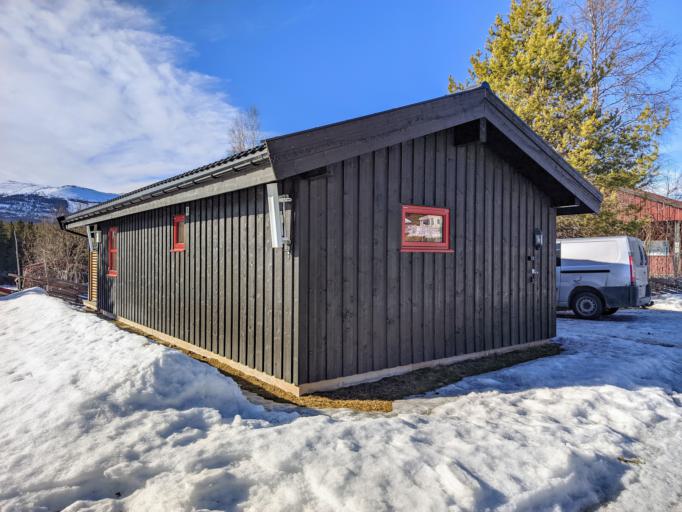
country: NO
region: Hedmark
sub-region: Trysil
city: Innbygda
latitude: 61.2922
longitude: 12.2838
